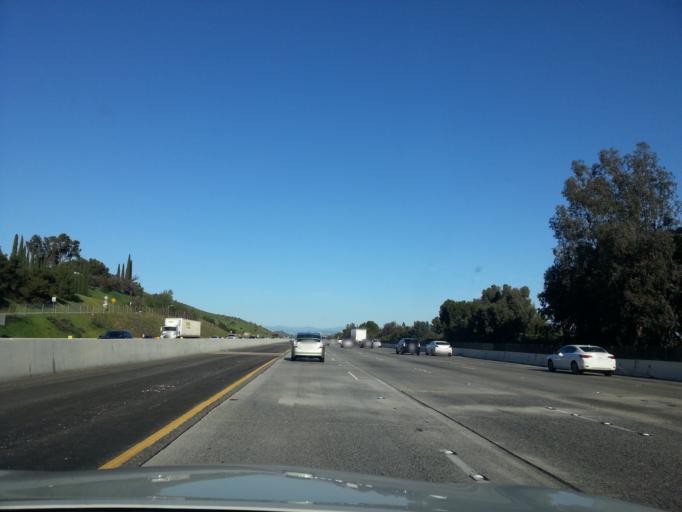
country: US
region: California
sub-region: Ventura County
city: Thousand Oaks
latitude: 34.1685
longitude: -118.8413
